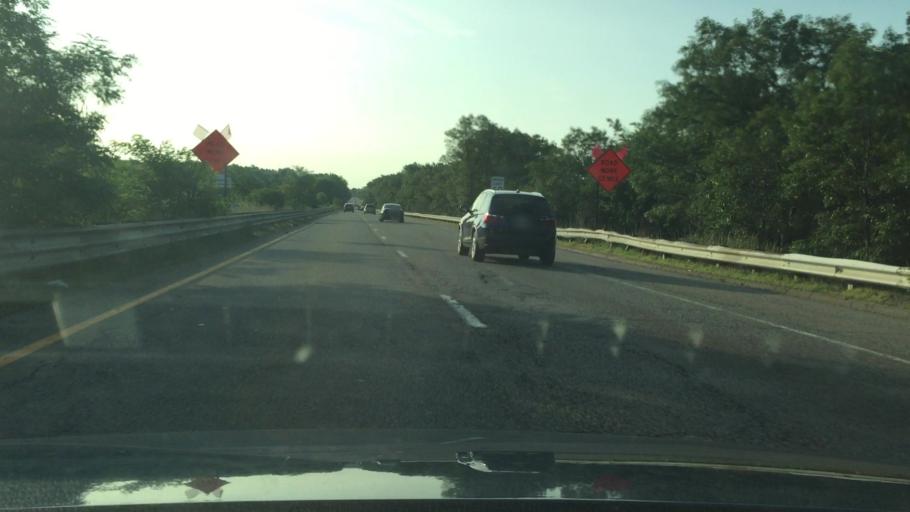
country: US
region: Massachusetts
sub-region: Plymouth County
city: Rockland
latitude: 42.1654
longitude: -70.8920
